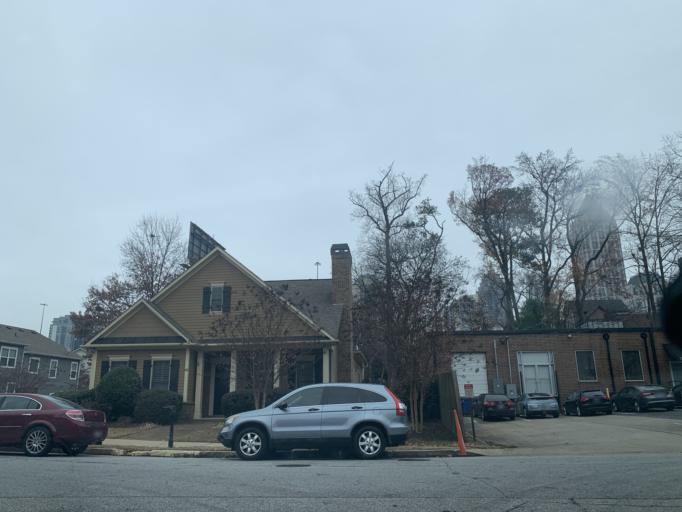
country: US
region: Georgia
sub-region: Fulton County
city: Atlanta
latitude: 33.7895
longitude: -84.3946
